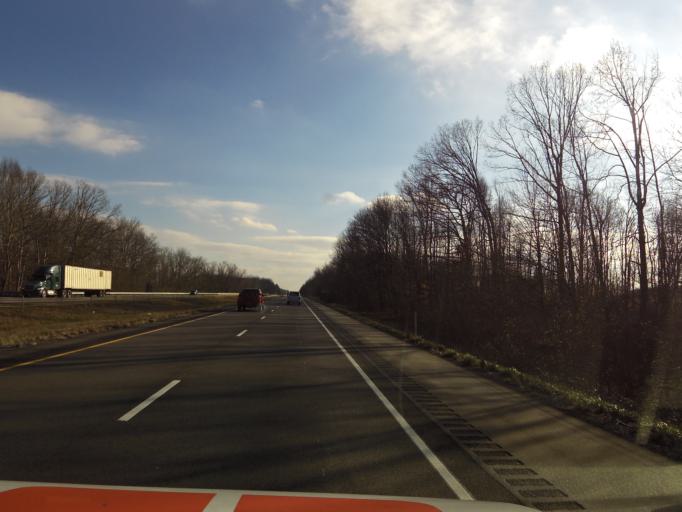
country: US
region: Indiana
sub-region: Scott County
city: Austin
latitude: 38.7663
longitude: -85.8315
